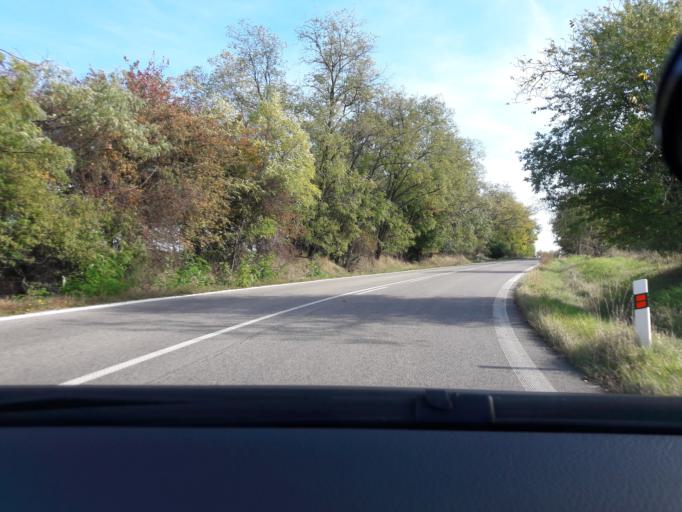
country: SK
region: Banskobystricky
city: Dudince
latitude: 48.2591
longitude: 18.7740
